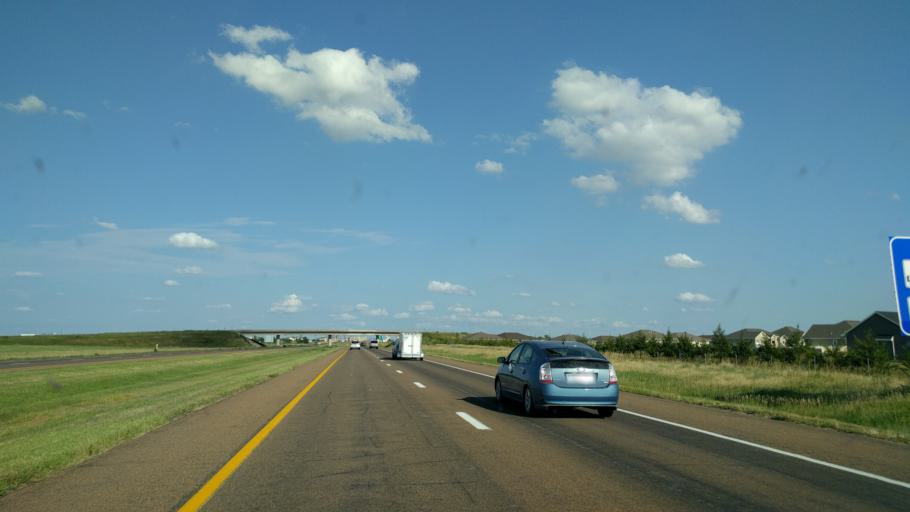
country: US
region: Kansas
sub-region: Ellis County
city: Hays
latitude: 38.9068
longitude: -99.3393
